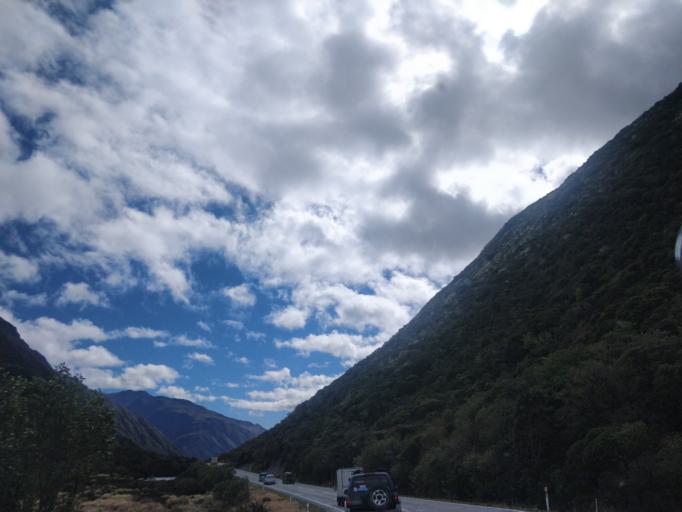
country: NZ
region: West Coast
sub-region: Grey District
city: Greymouth
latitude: -42.9028
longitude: 171.5604
